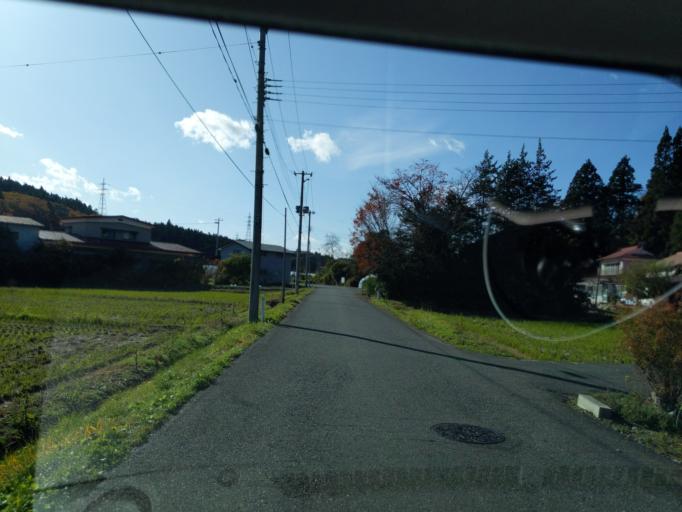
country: JP
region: Iwate
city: Mizusawa
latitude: 39.0935
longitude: 141.1305
